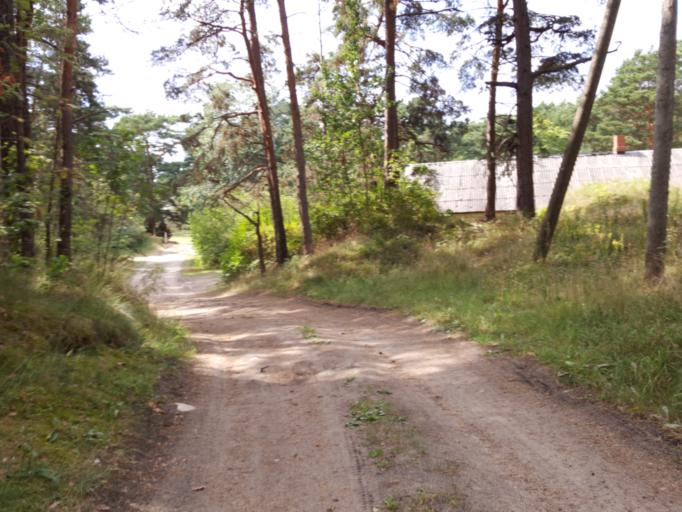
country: LV
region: Salacgrivas
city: Ainazi
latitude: 57.8582
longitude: 24.3506
